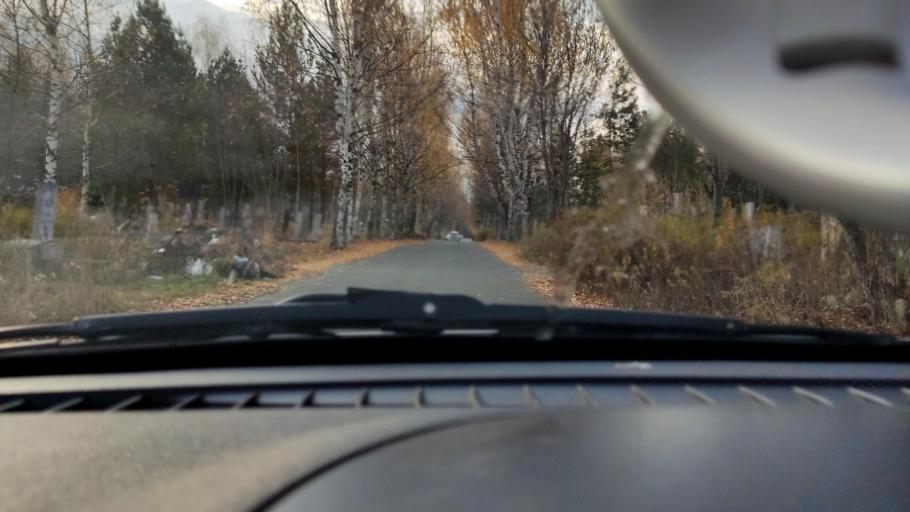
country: RU
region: Perm
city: Kondratovo
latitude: 58.0656
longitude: 56.1331
